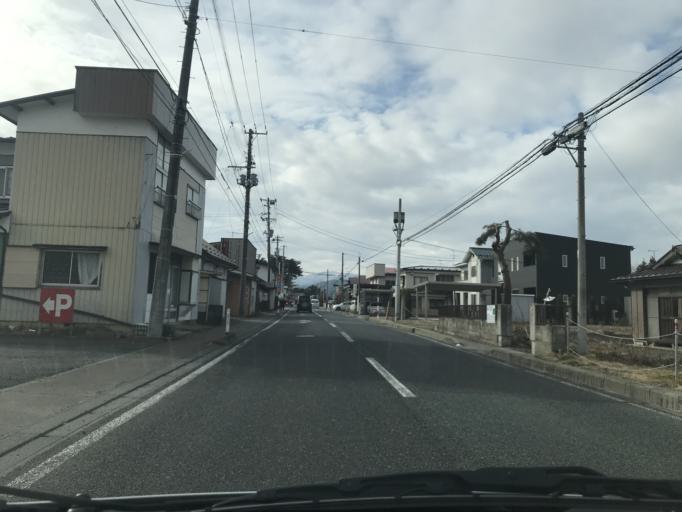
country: JP
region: Iwate
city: Hanamaki
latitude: 39.4092
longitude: 141.1016
